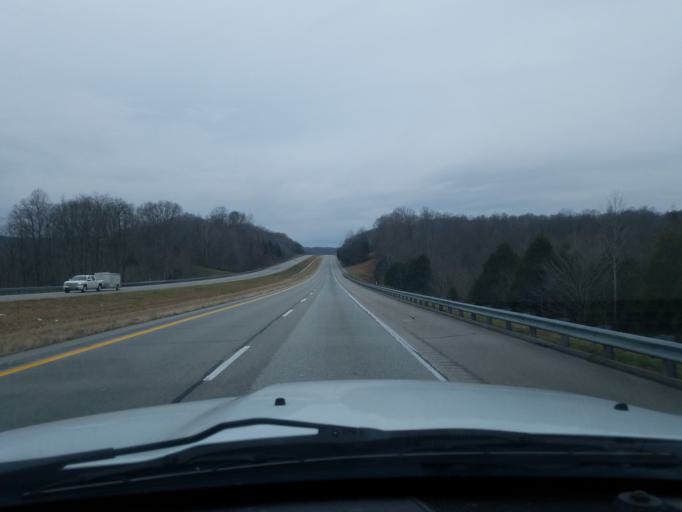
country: US
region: Indiana
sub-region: Crawford County
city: English
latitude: 38.2541
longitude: -86.3115
